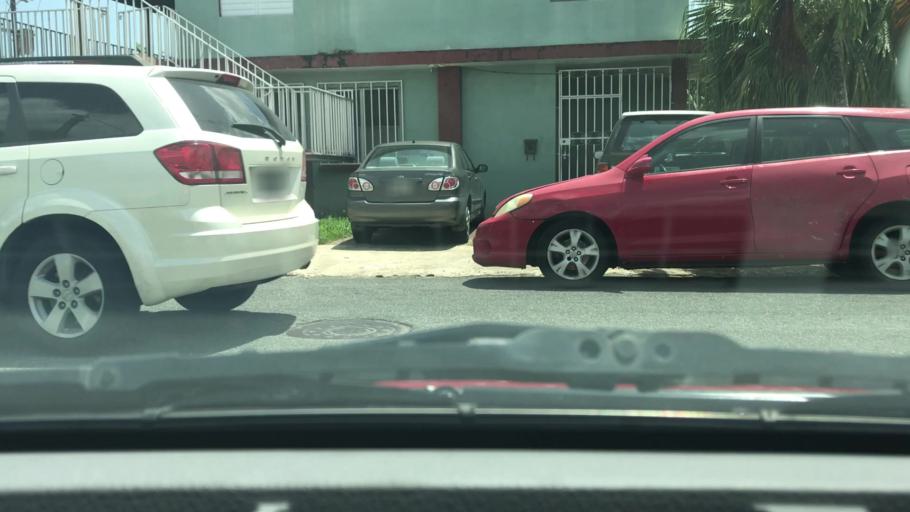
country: PR
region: Bayamon
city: Bayamon
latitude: 18.3903
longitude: -66.1403
